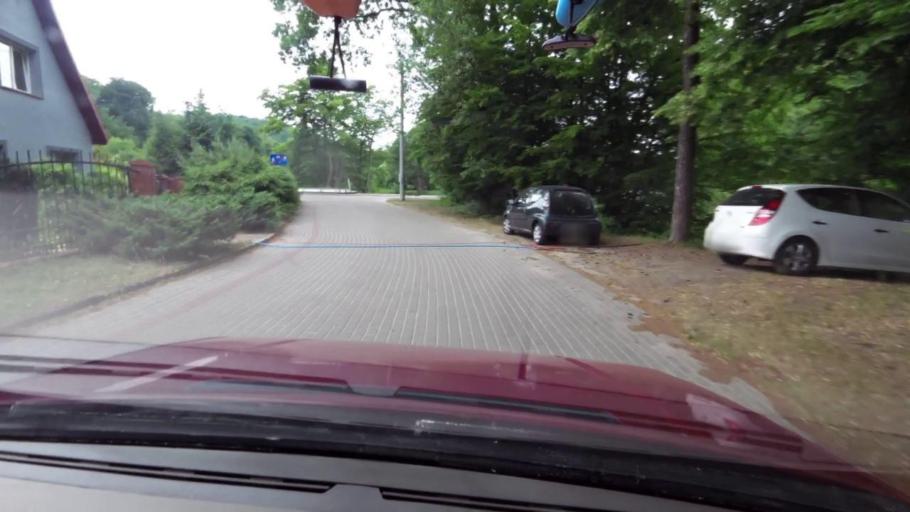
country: PL
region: Pomeranian Voivodeship
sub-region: Powiat slupski
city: Kepice
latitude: 54.2448
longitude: 16.8944
